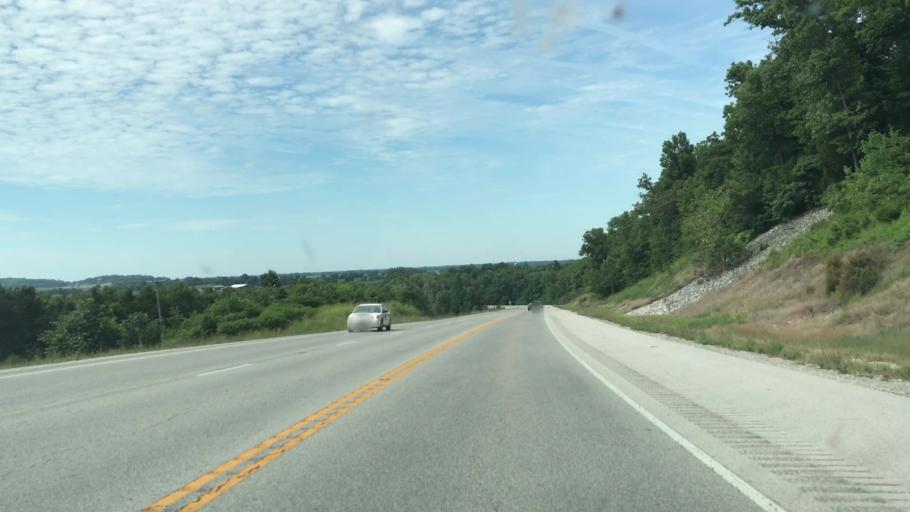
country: US
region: Kentucky
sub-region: Edmonson County
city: Brownsville
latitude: 37.0989
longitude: -86.2308
